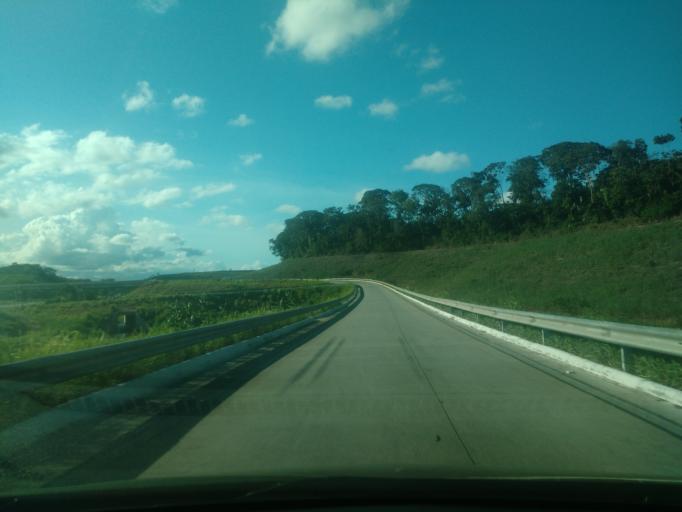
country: BR
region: Alagoas
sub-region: Messias
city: Messias
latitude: -9.3703
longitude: -35.8303
